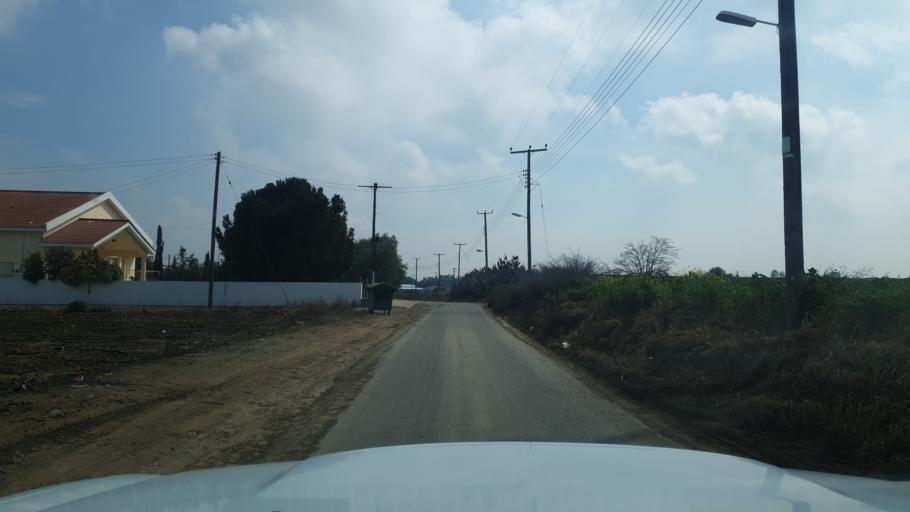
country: CY
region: Lefkosia
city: Kato Deftera
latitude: 35.0798
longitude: 33.2781
